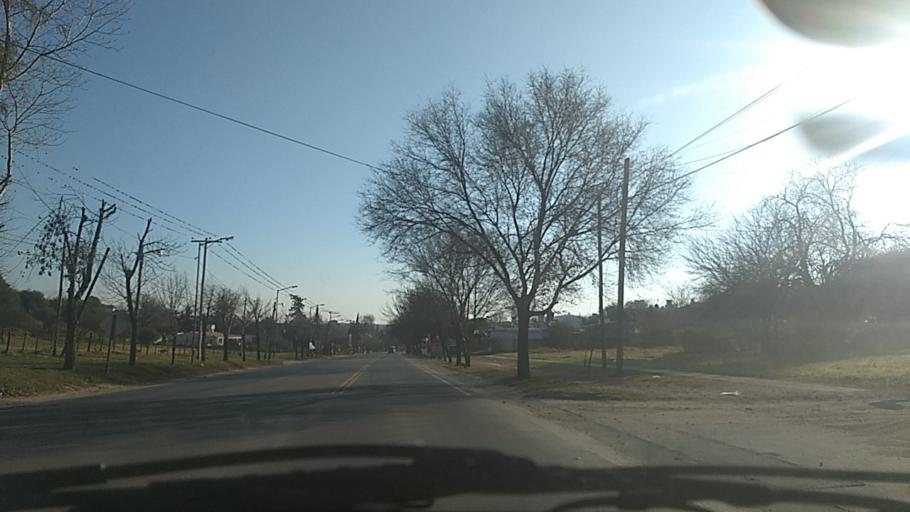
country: AR
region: Cordoba
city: Salsipuedes
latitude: -31.1243
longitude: -64.2941
